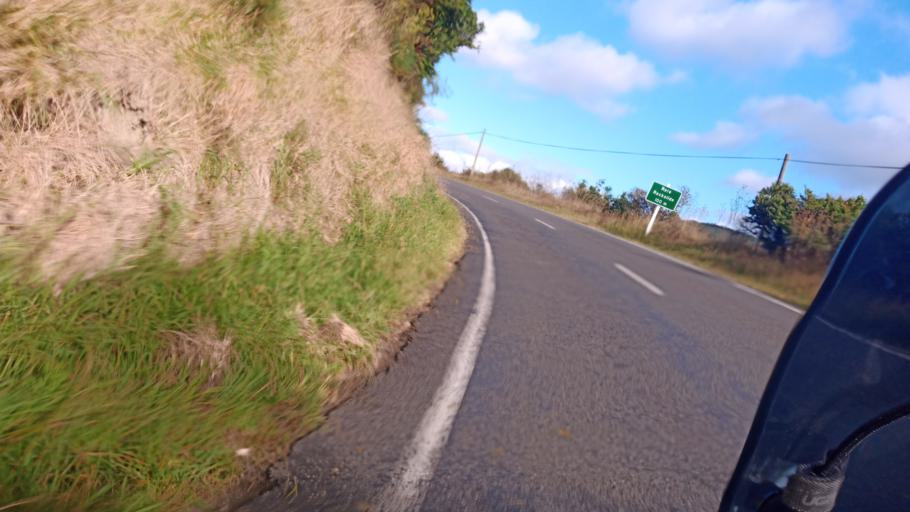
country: NZ
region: Gisborne
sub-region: Gisborne District
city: Gisborne
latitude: -38.5390
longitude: 177.5931
